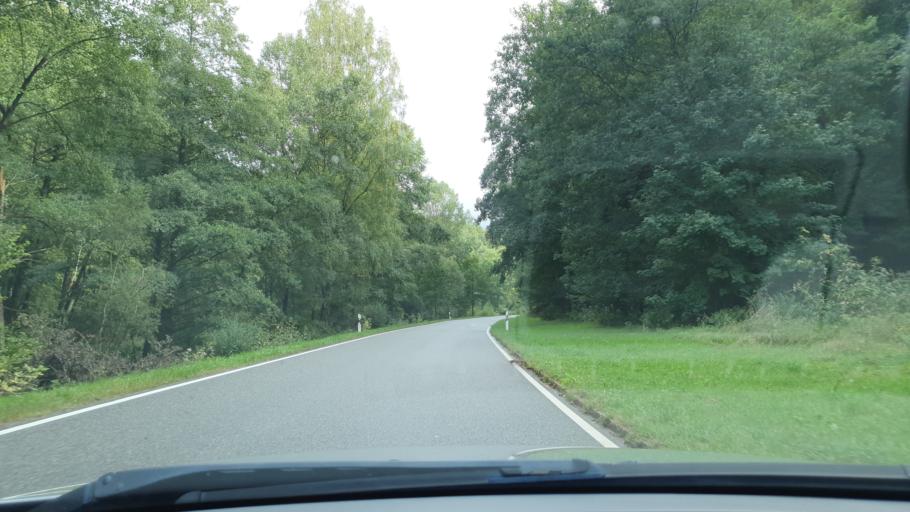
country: DE
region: Rheinland-Pfalz
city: Gerhardsbrunn
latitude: 49.3430
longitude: 7.5161
